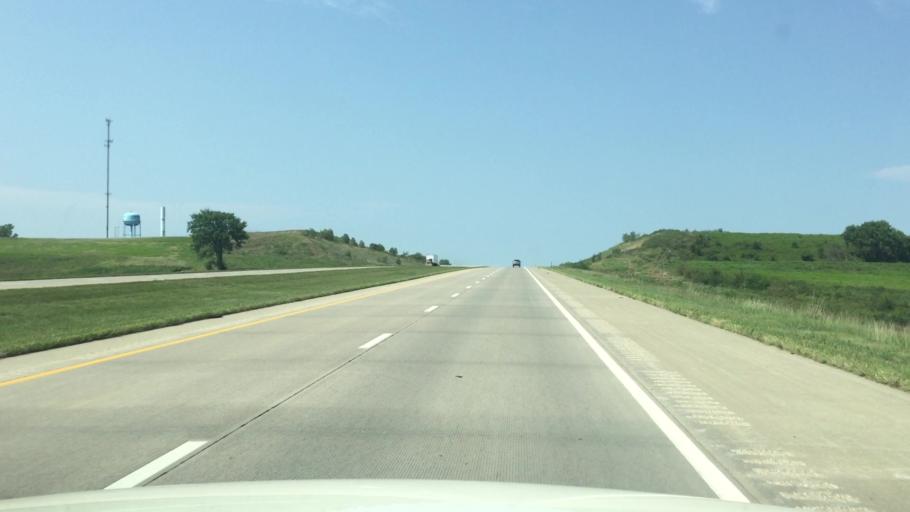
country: US
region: Kansas
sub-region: Linn County
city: Pleasanton
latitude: 38.1032
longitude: -94.7134
